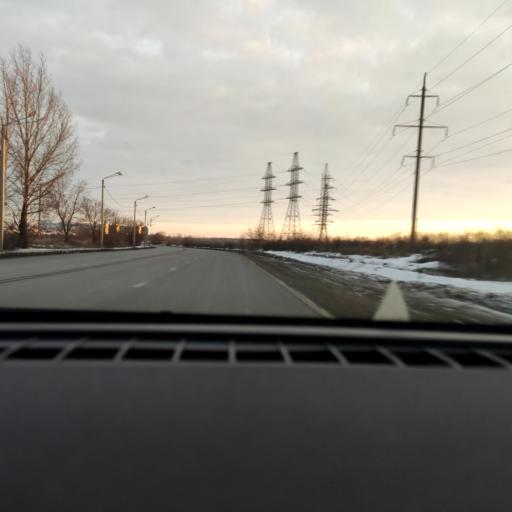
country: RU
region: Voronezj
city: Maslovka
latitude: 51.6206
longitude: 39.2756
